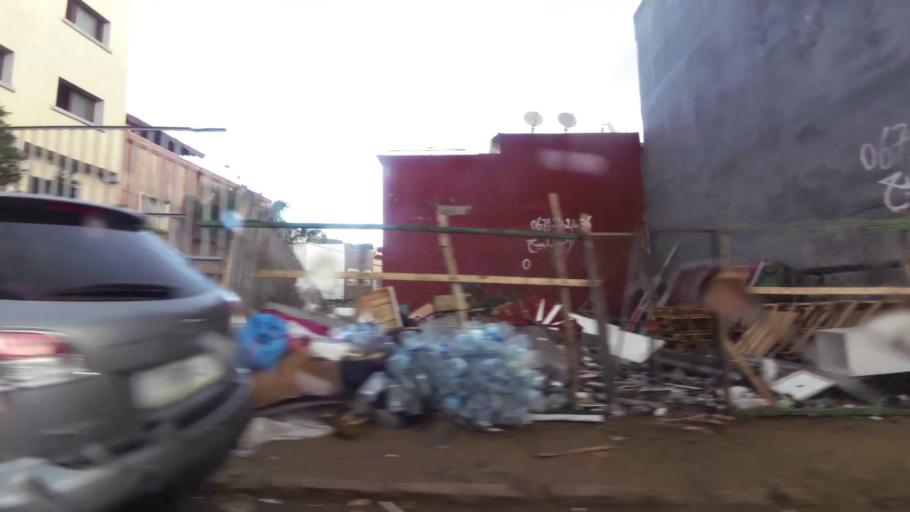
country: MA
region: Grand Casablanca
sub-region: Casablanca
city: Casablanca
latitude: 33.5370
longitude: -7.6702
